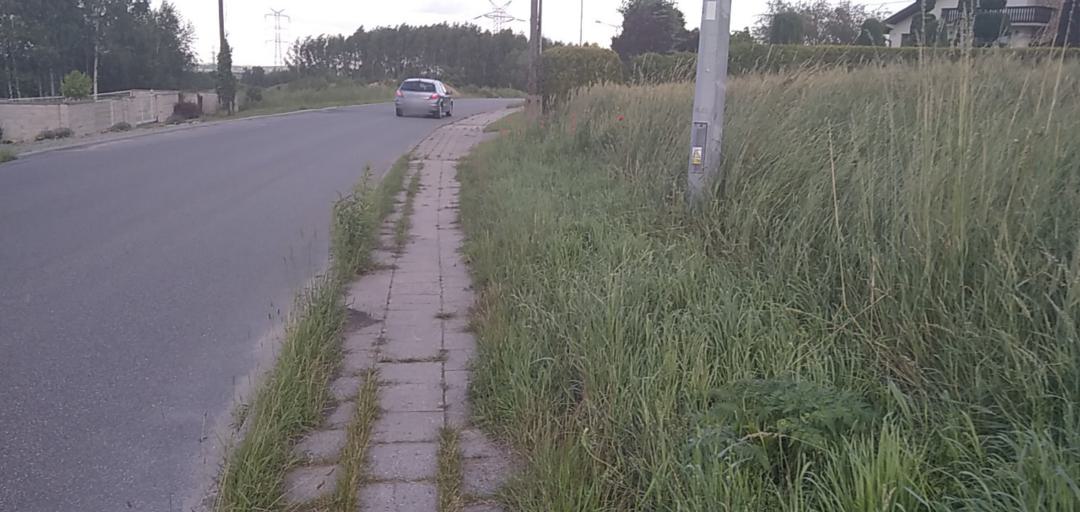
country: PL
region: Silesian Voivodeship
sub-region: Powiat bedzinski
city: Mierzecice
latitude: 50.4097
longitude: 19.1387
